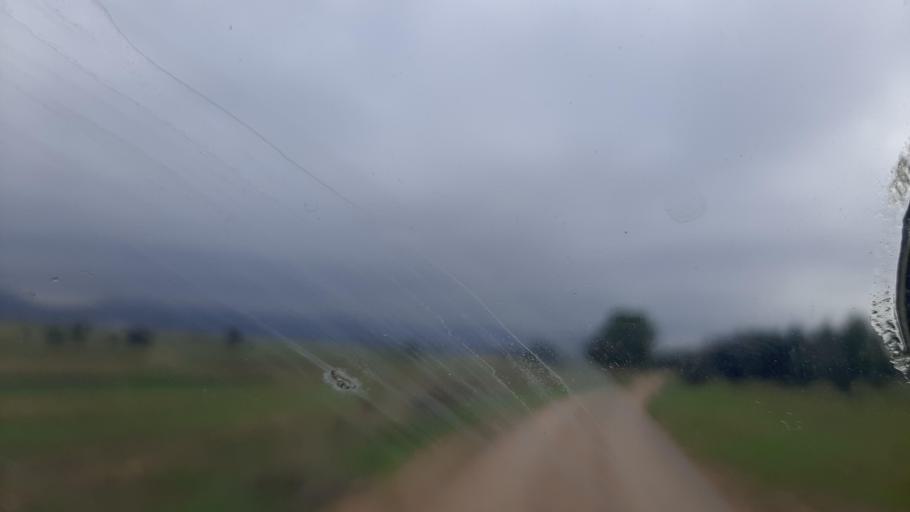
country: TN
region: Tunis
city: La Sebala du Mornag
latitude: 36.5711
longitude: 10.2941
